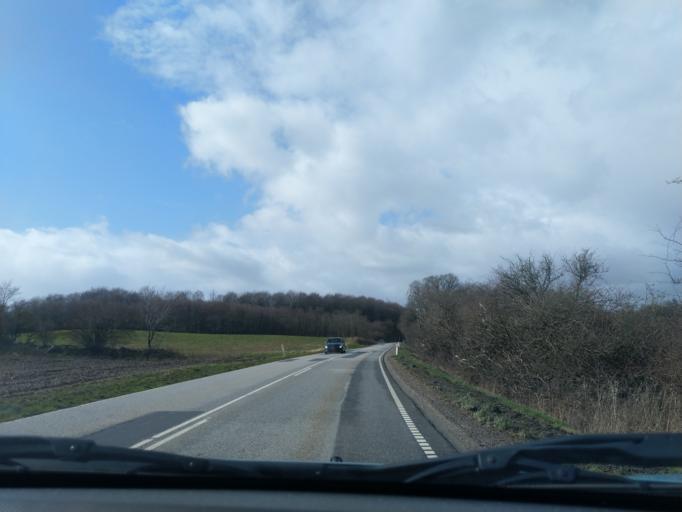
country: DK
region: Zealand
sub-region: Naestved Kommune
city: Fuglebjerg
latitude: 55.3213
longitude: 11.6176
